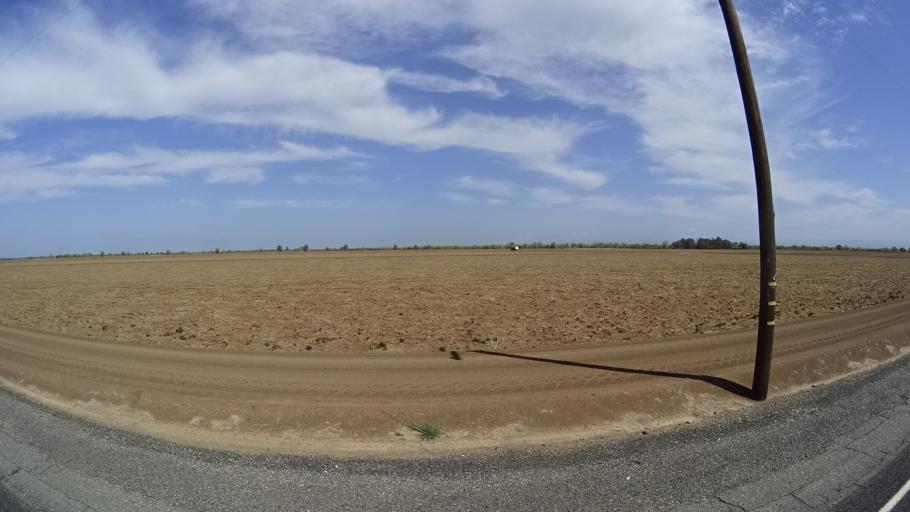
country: US
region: California
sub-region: Butte County
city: Durham
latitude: 39.5364
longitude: -121.9156
